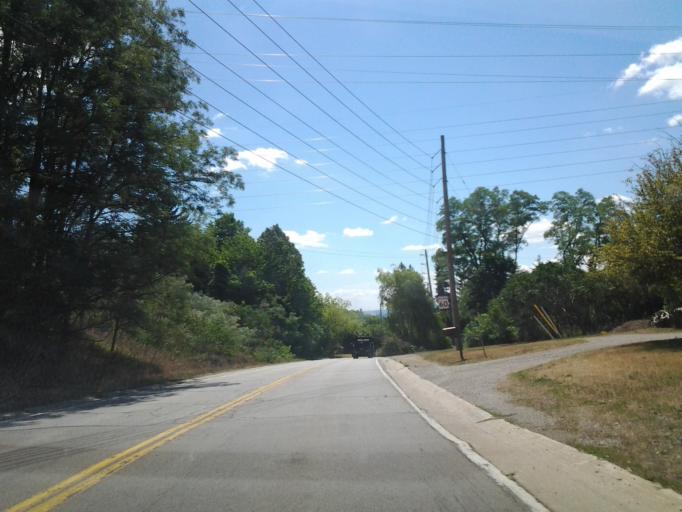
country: CA
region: Ontario
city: Burlington
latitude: 43.3264
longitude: -79.8802
